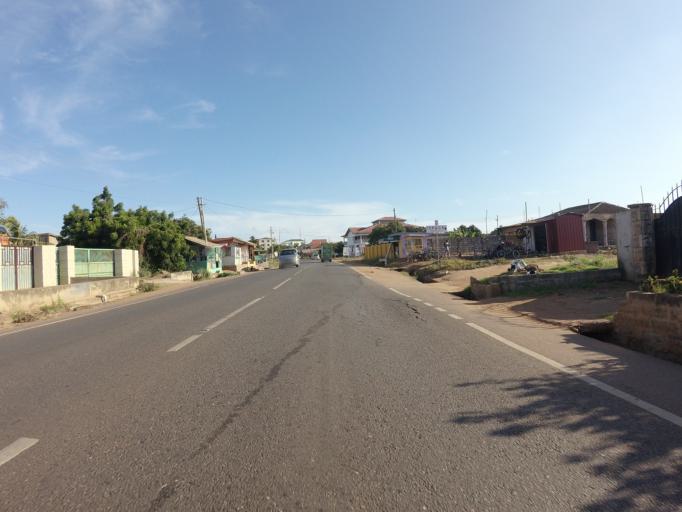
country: GH
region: Greater Accra
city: Nungua
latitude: 5.6396
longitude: -0.0925
